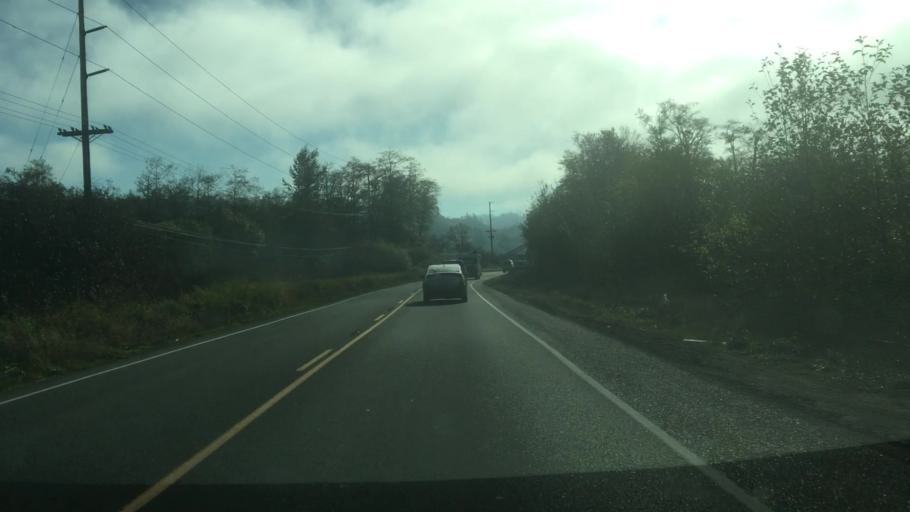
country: US
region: Washington
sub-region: Grays Harbor County
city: Montesano
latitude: 46.9724
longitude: -123.6011
